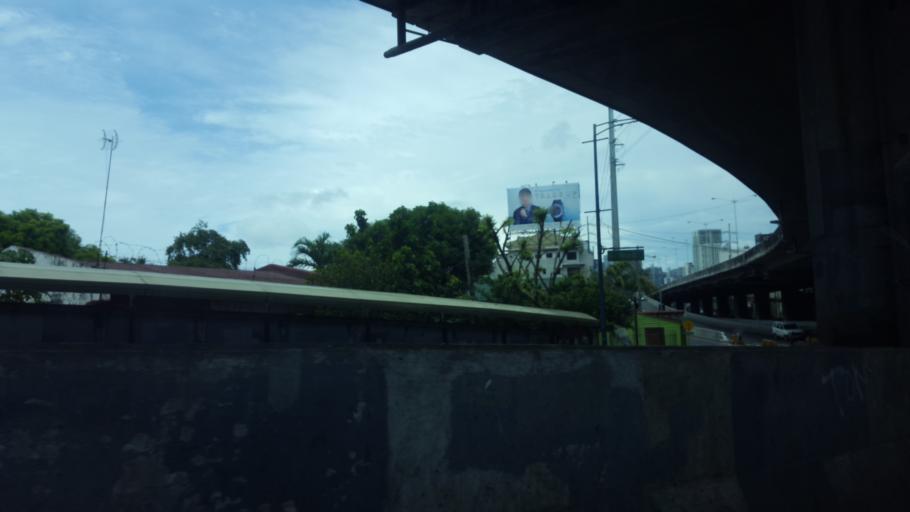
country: PH
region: Metro Manila
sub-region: Makati City
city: Makati City
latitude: 14.5557
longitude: 121.0440
